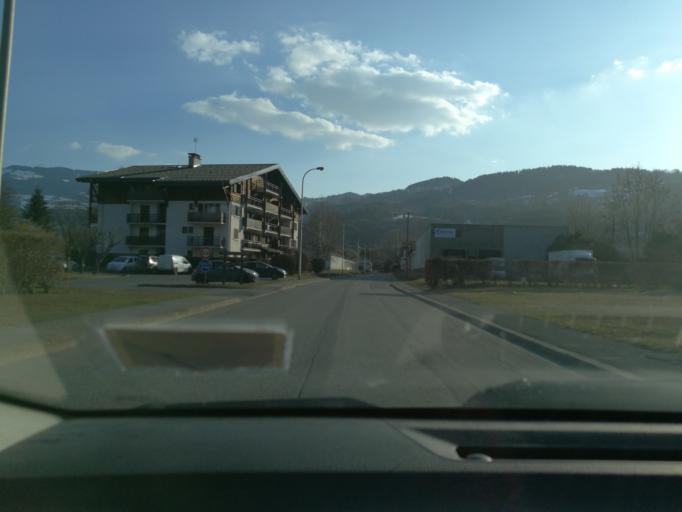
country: FR
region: Rhone-Alpes
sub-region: Departement de la Haute-Savoie
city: Sallanches
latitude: 45.9344
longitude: 6.6385
